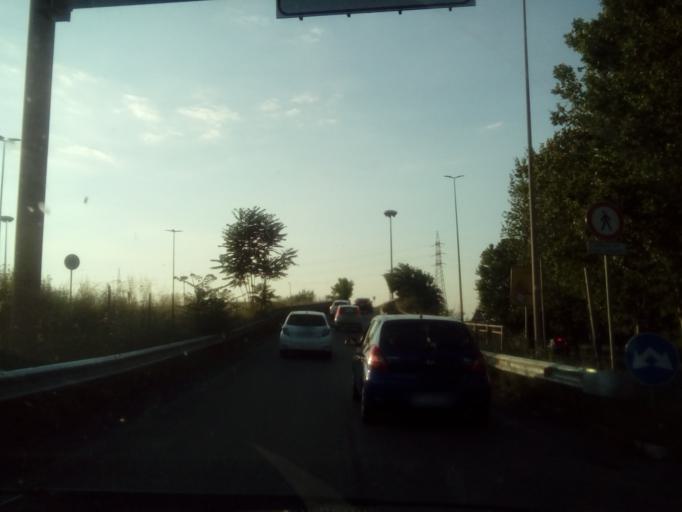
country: IT
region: Latium
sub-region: Citta metropolitana di Roma Capitale
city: Rome
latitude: 41.9017
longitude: 12.5753
